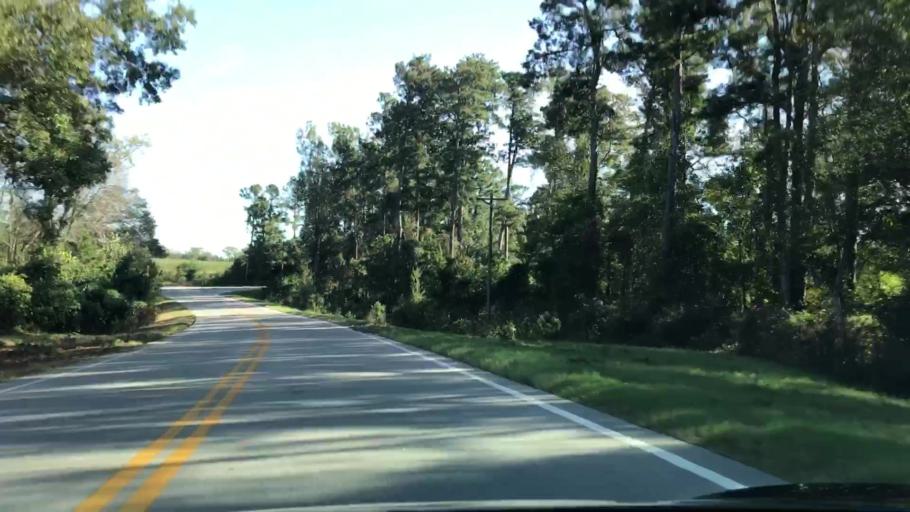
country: US
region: Georgia
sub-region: Glascock County
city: Gibson
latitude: 33.3214
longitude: -82.5578
